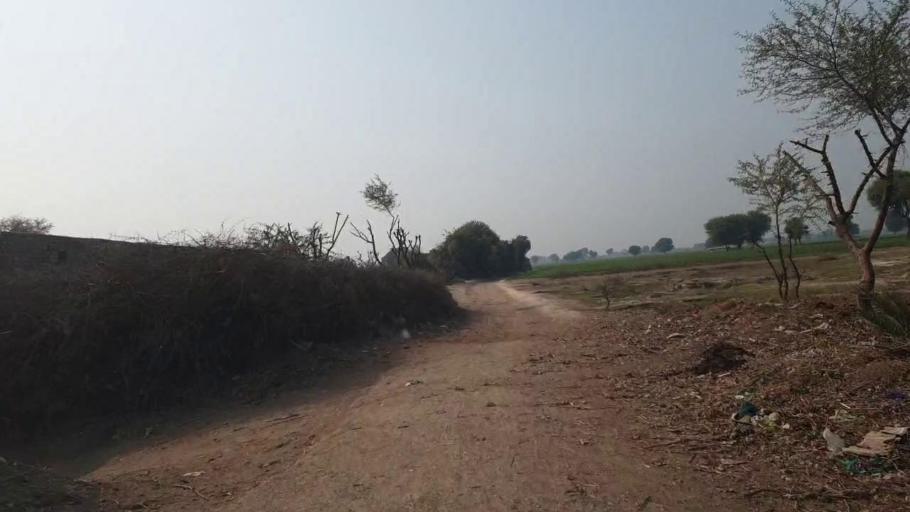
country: PK
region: Sindh
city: Hala
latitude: 25.8469
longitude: 68.4395
